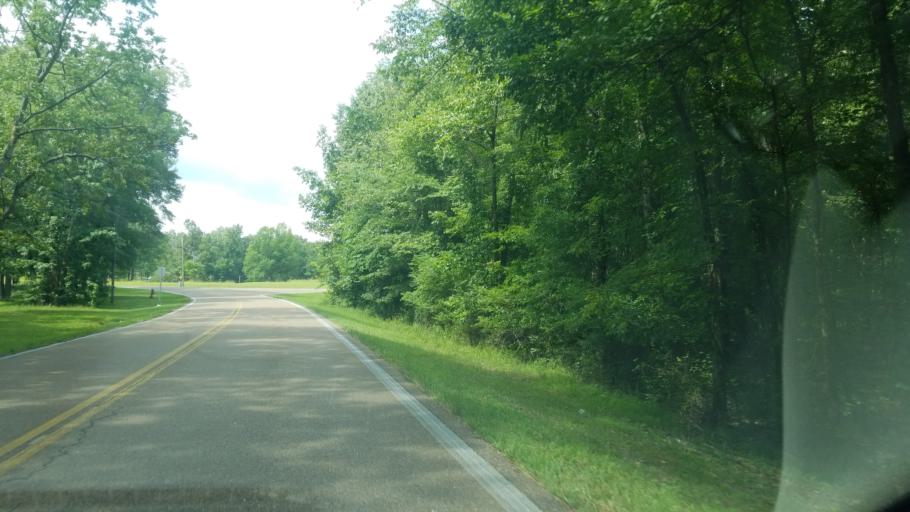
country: US
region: Tennessee
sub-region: Hamilton County
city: Lakesite
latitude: 35.1748
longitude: -85.1161
